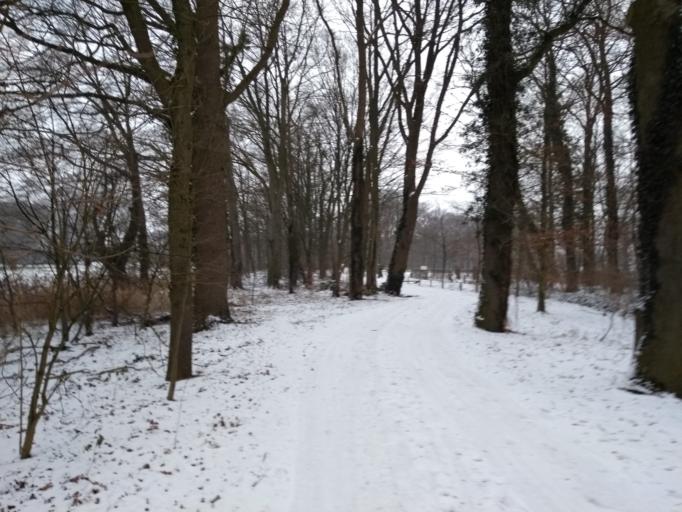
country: NL
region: Overijssel
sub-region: Gemeente Borne
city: Borne
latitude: 52.3248
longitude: 6.7447
